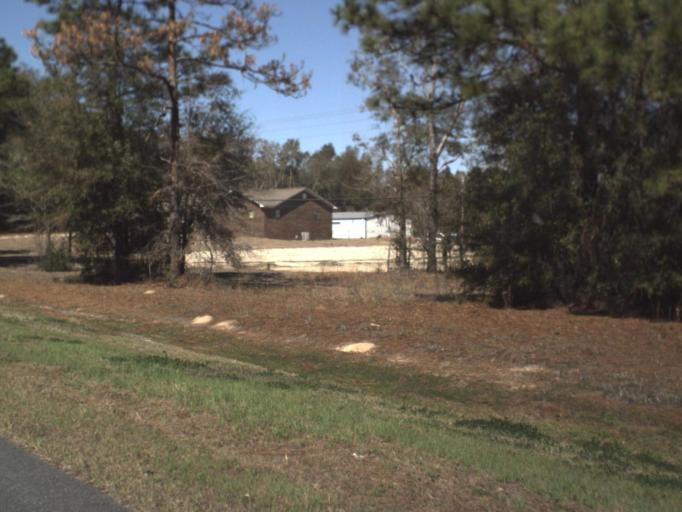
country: US
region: Florida
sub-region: Jackson County
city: Marianna
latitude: 30.7364
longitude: -85.1074
